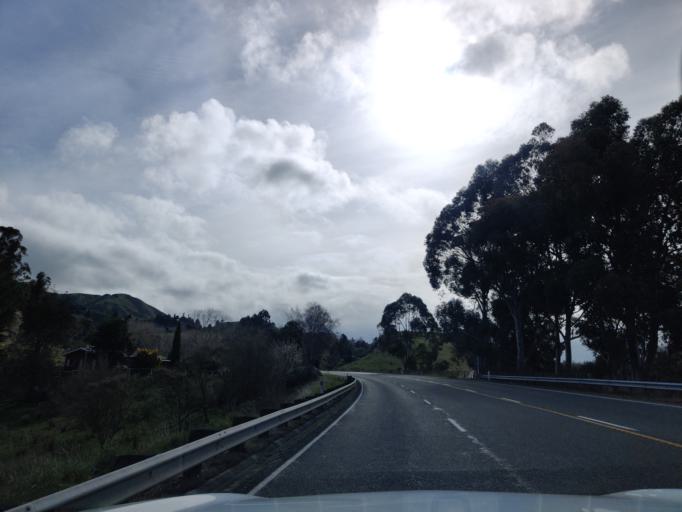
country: NZ
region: Manawatu-Wanganui
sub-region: Ruapehu District
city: Waiouru
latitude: -39.8047
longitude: 175.7981
